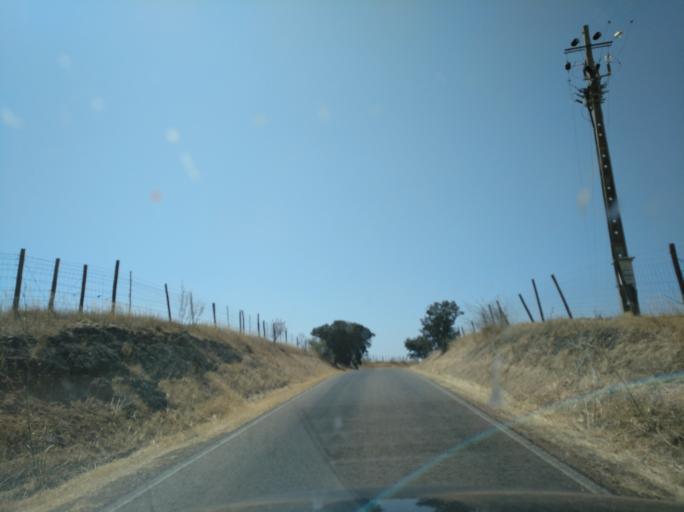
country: PT
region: Portalegre
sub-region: Campo Maior
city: Campo Maior
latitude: 39.0067
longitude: -6.9830
